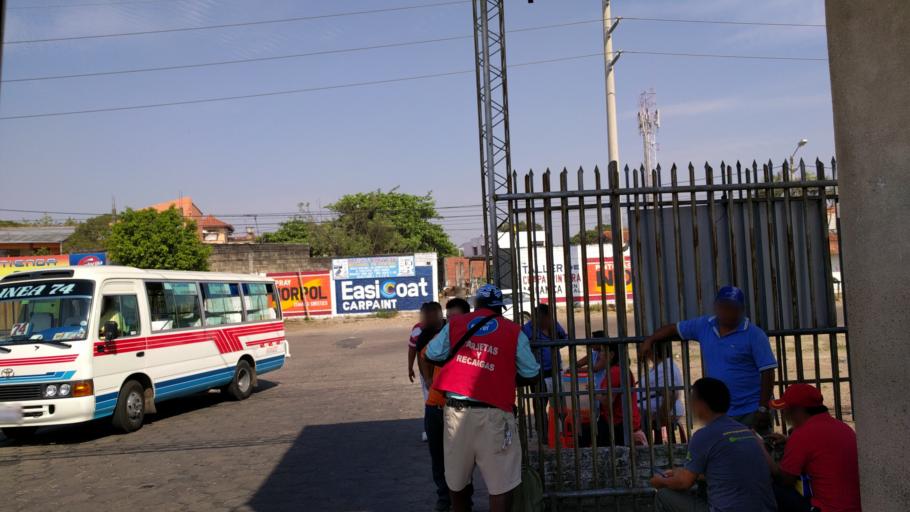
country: BO
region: Santa Cruz
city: Santa Cruz de la Sierra
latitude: -17.8112
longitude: -63.1748
